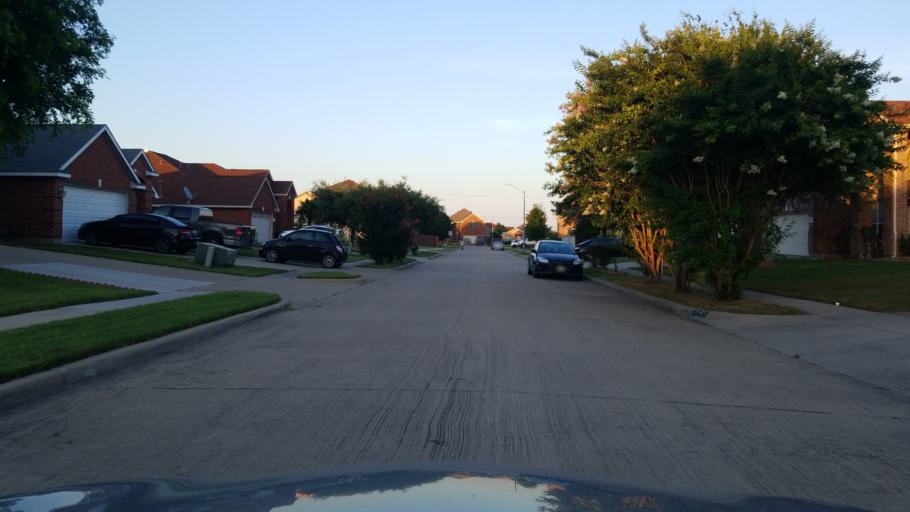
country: US
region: Texas
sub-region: Dallas County
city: Grand Prairie
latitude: 32.6873
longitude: -97.0386
